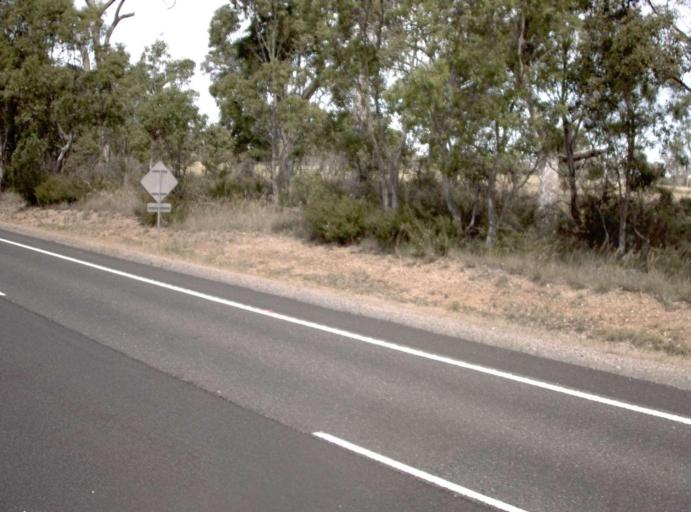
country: AU
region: Victoria
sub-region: Wellington
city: Sale
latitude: -37.9249
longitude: 147.2294
